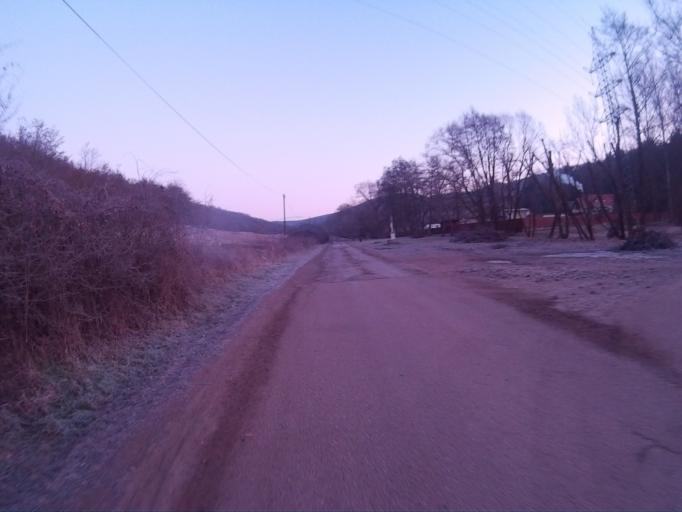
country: HU
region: Borsod-Abauj-Zemplen
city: Putnok
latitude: 48.3068
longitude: 20.4375
